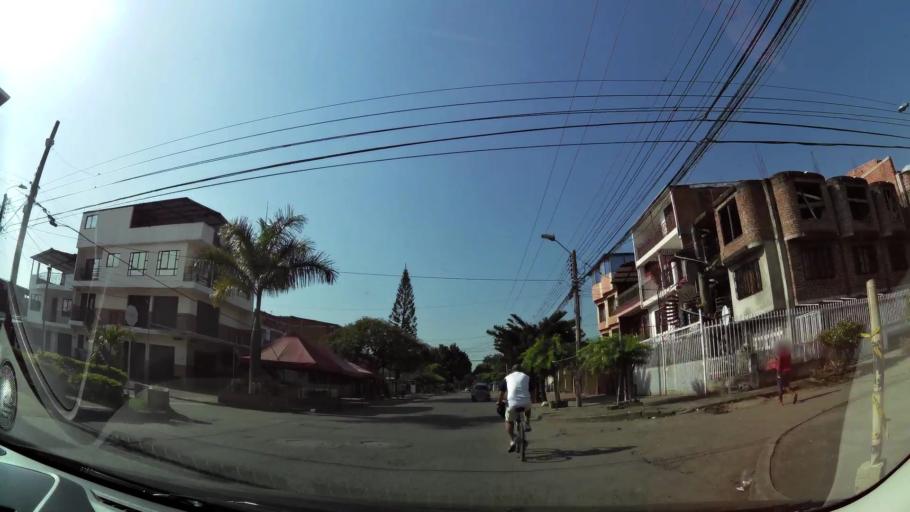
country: CO
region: Valle del Cauca
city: Cali
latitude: 3.4227
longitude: -76.5121
